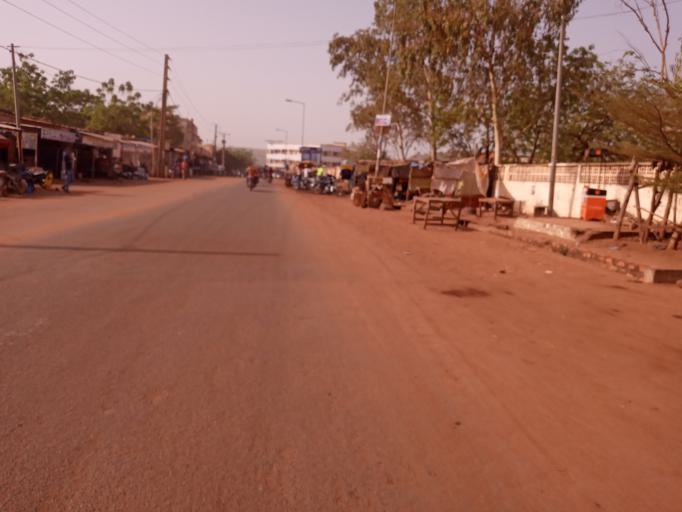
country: ML
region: Bamako
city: Bamako
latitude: 12.6777
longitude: -7.9440
